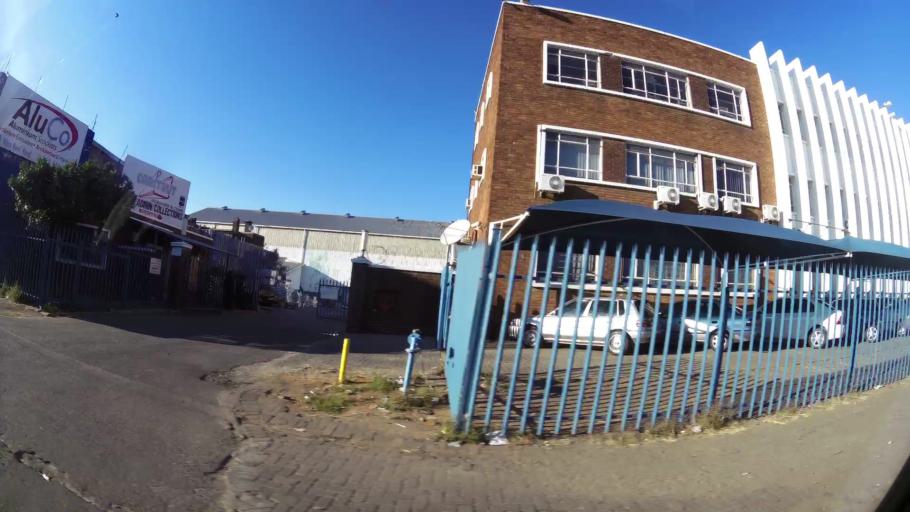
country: ZA
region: Gauteng
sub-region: City of Johannesburg Metropolitan Municipality
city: Johannesburg
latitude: -26.2067
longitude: 28.0969
